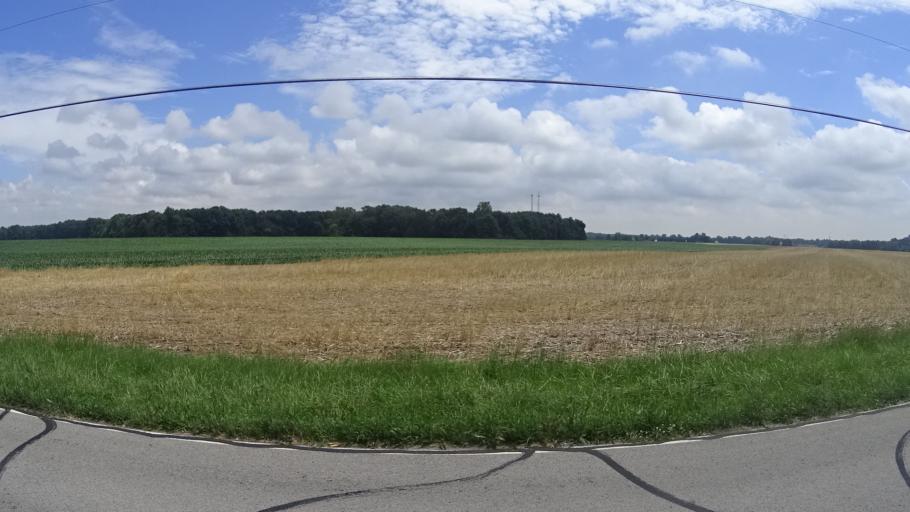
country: US
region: Ohio
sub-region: Erie County
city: Milan
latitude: 41.3121
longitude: -82.5738
